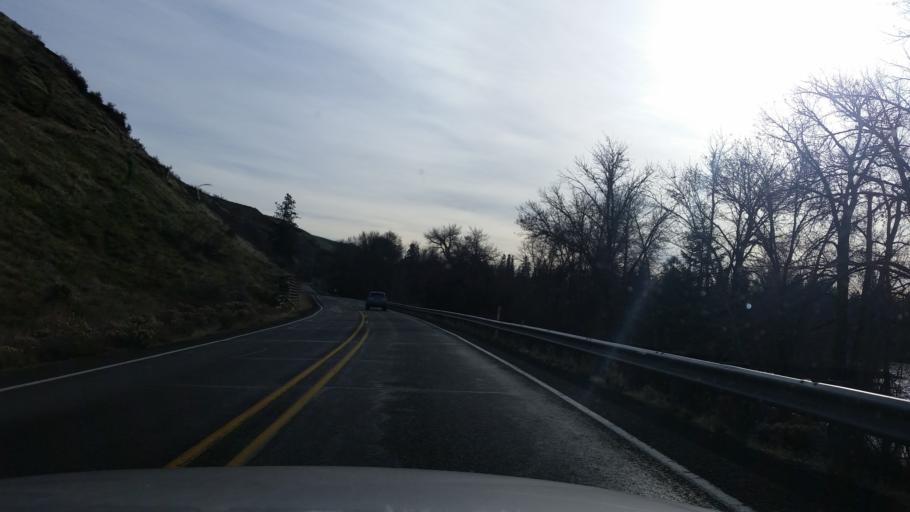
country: US
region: Washington
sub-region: Kittitas County
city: Ellensburg
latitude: 47.0784
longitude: -120.6696
